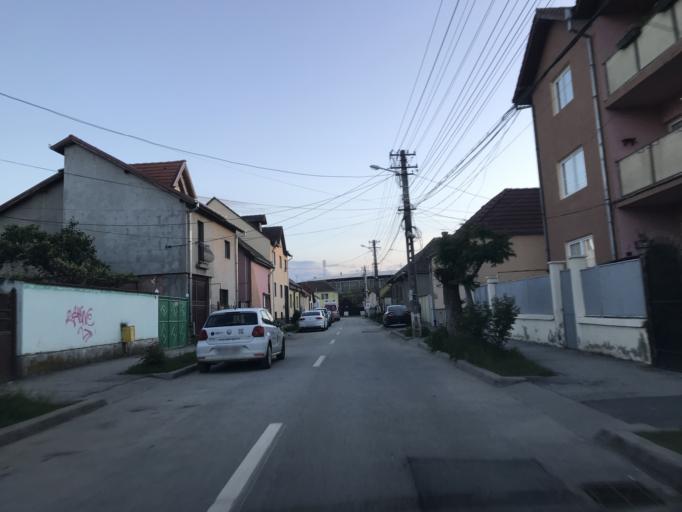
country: RO
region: Sibiu
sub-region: Municipiul Sibiu
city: Sibiu
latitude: 45.7974
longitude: 24.1705
